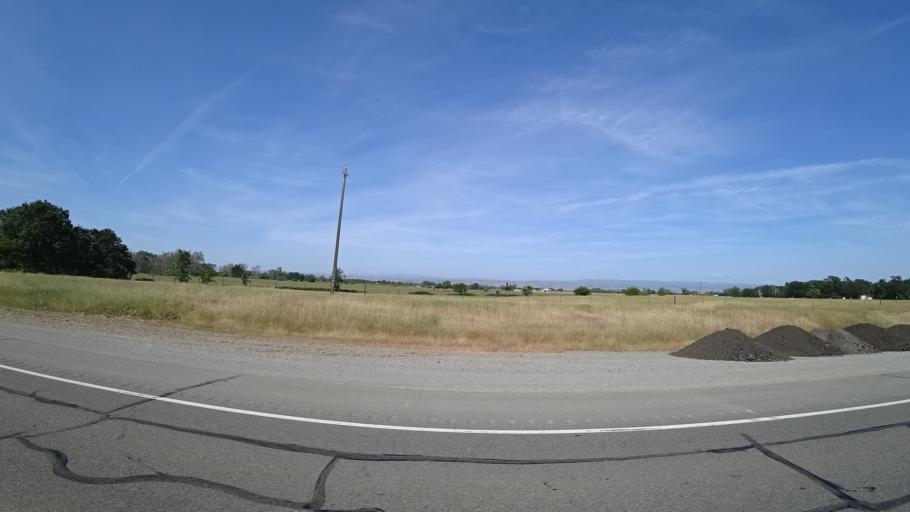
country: US
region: California
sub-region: Tehama County
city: Los Molinos
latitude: 39.9421
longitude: -122.0484
